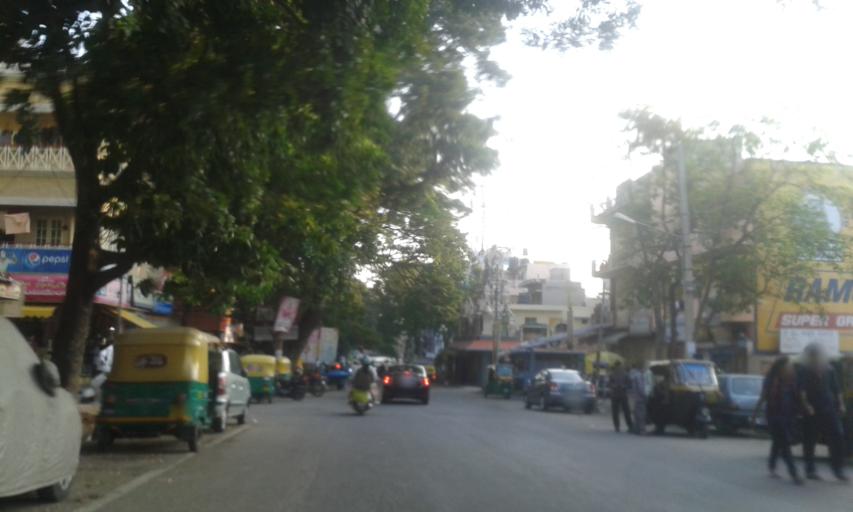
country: IN
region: Karnataka
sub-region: Bangalore Urban
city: Bangalore
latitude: 12.9194
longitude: 77.5896
